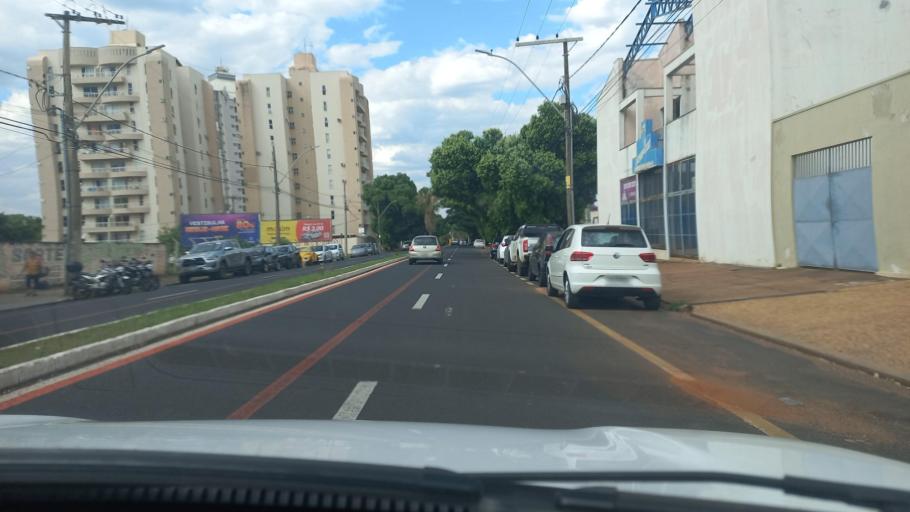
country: BR
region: Minas Gerais
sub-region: Uberaba
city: Uberaba
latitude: -19.7624
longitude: -47.9589
